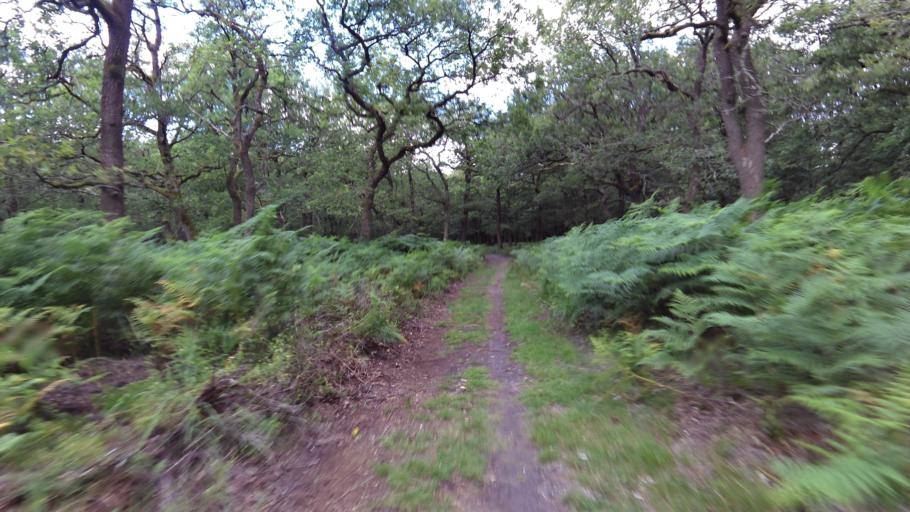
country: NL
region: Gelderland
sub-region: Gemeente Apeldoorn
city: Uddel
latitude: 52.2388
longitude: 5.8179
